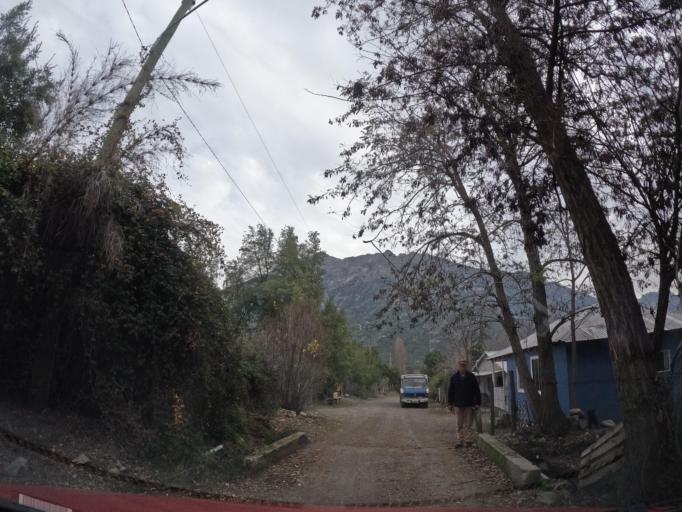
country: CL
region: Maule
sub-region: Provincia de Linares
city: Colbun
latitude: -35.7248
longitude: -71.0186
